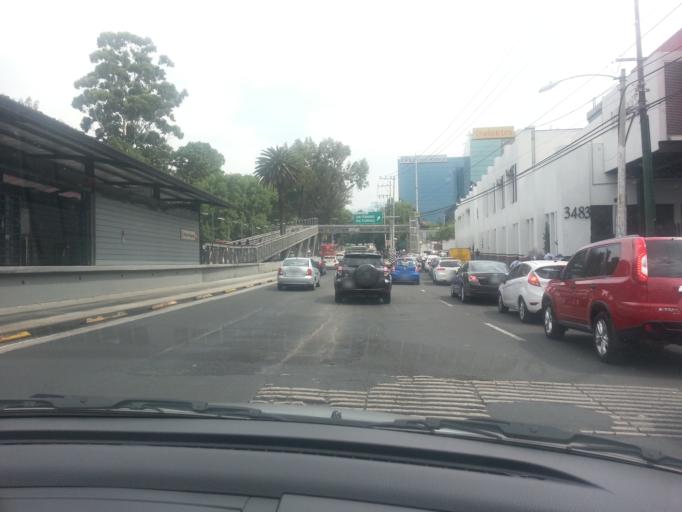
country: MX
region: Mexico City
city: Tlalpan
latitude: 19.2992
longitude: -99.1857
